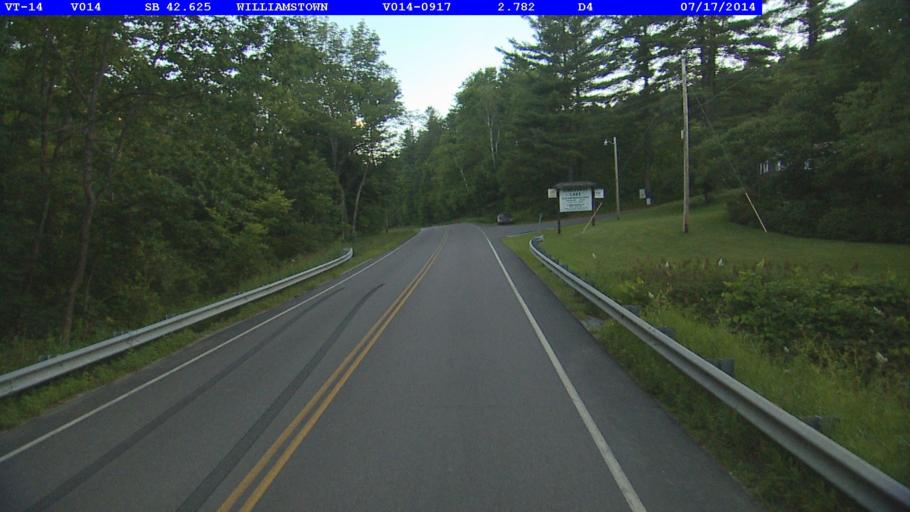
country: US
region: Vermont
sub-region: Orange County
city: Williamstown
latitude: 44.0990
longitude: -72.5468
